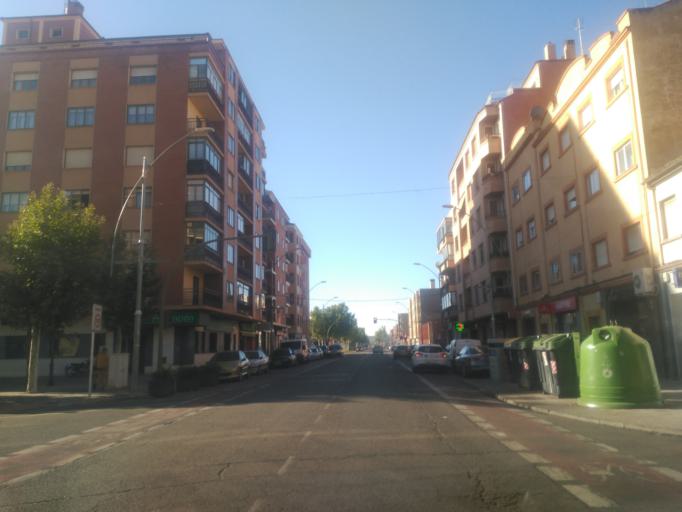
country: ES
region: Castille and Leon
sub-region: Provincia de Burgos
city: Aranda de Duero
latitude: 41.6659
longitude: -3.6912
